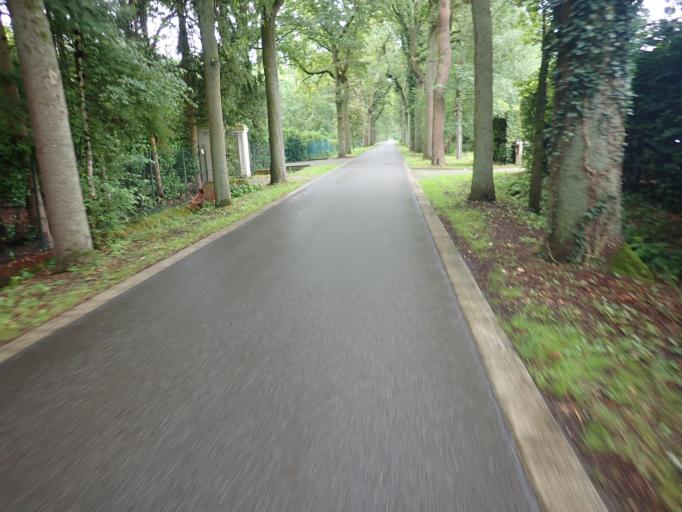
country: BE
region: Flanders
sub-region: Provincie Antwerpen
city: Zoersel
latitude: 51.2531
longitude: 4.7005
